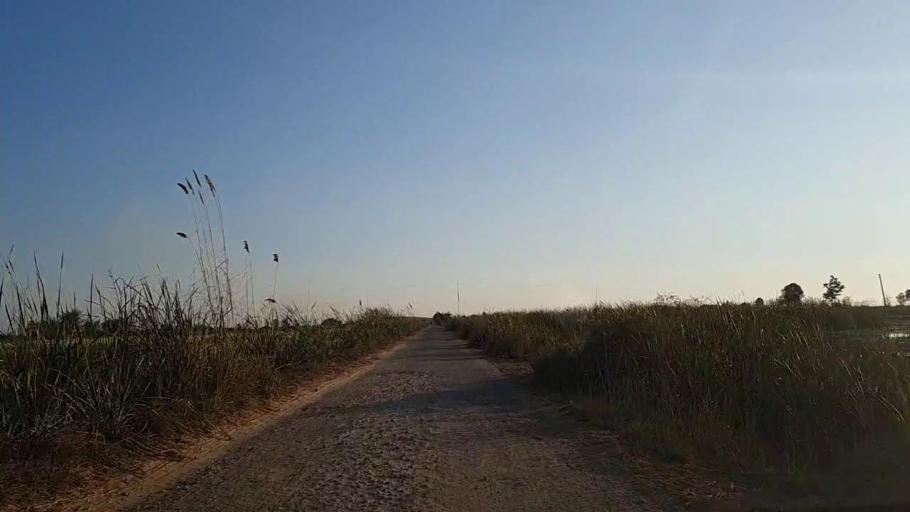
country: PK
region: Sindh
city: Khadro
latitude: 26.2718
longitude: 68.8099
